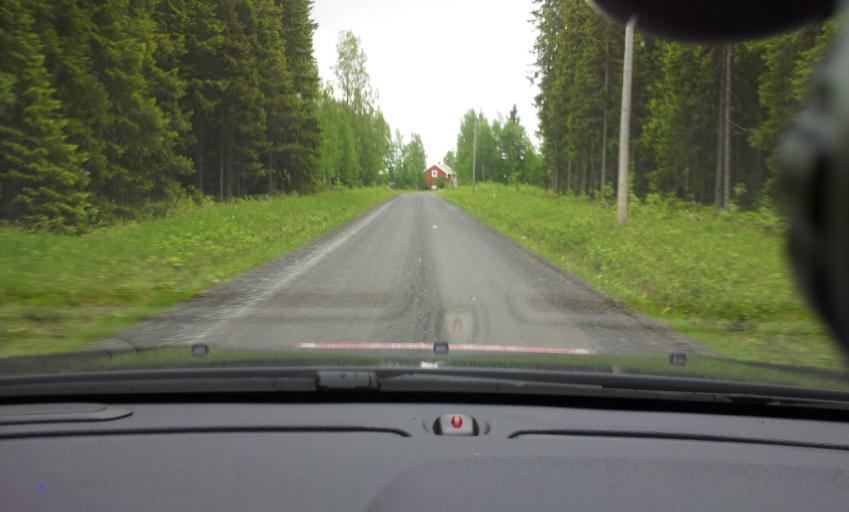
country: SE
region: Jaemtland
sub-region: OEstersunds Kommun
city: Brunflo
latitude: 63.1590
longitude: 15.0116
